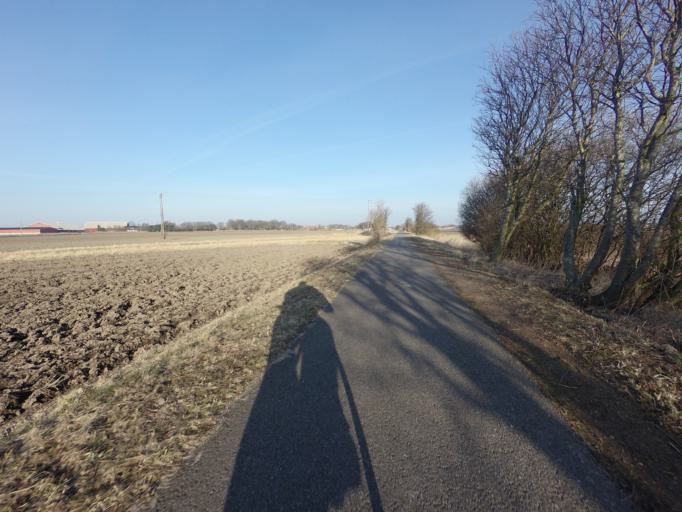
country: SE
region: Skane
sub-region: Hoganas Kommun
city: Hoganas
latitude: 56.1971
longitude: 12.5959
